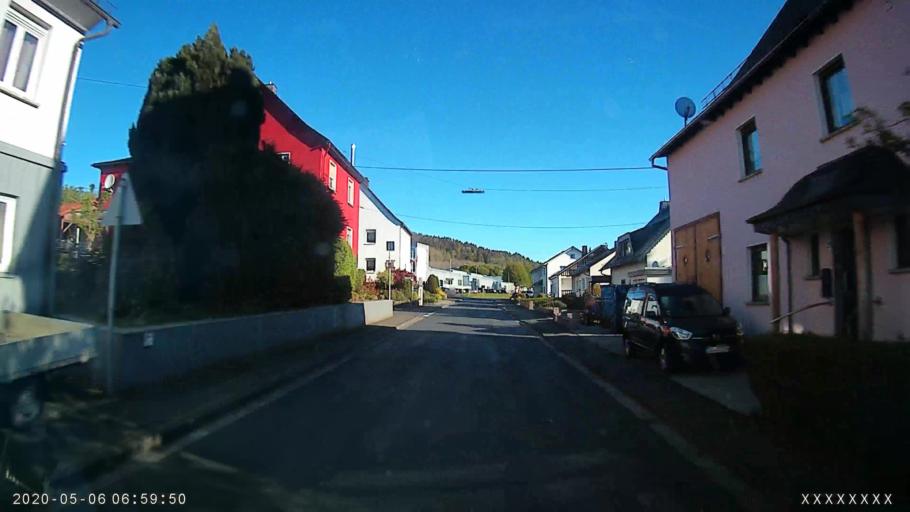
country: DE
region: Hesse
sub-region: Regierungsbezirk Giessen
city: Haiger
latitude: 50.7733
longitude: 8.2080
